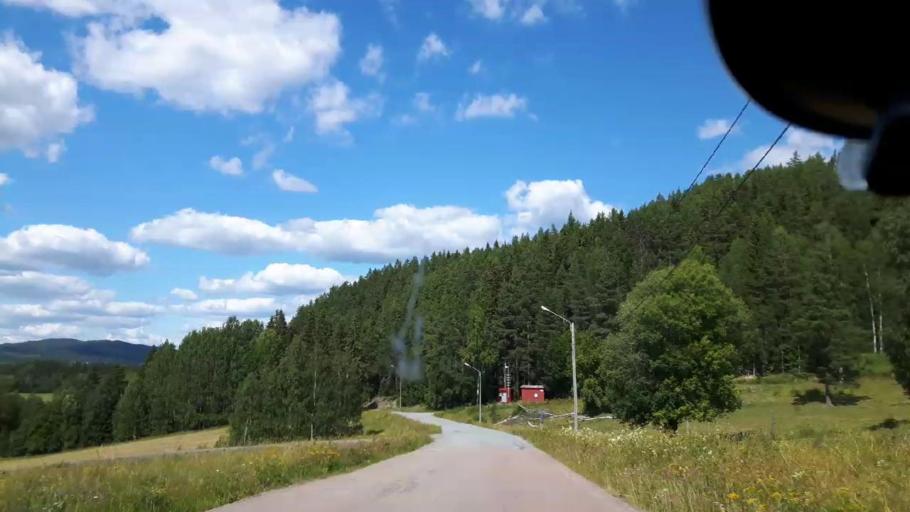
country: SE
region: Jaemtland
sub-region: Ragunda Kommun
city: Hammarstrand
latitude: 62.9551
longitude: 16.6834
